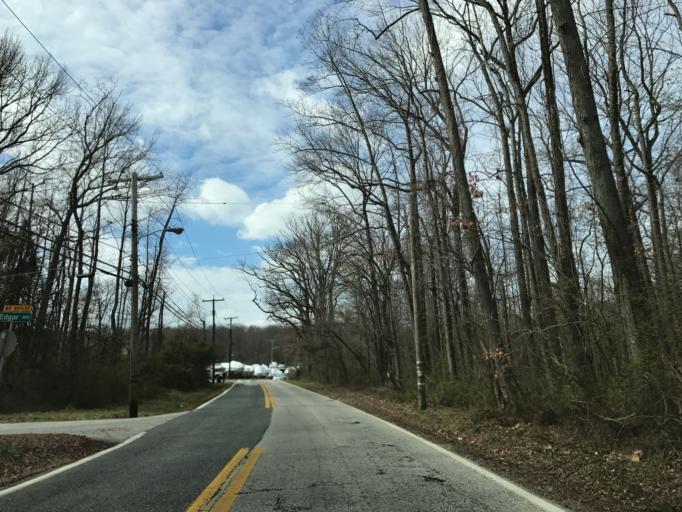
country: US
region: Maryland
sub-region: Baltimore County
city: Bowleys Quarters
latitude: 39.2953
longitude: -76.4092
